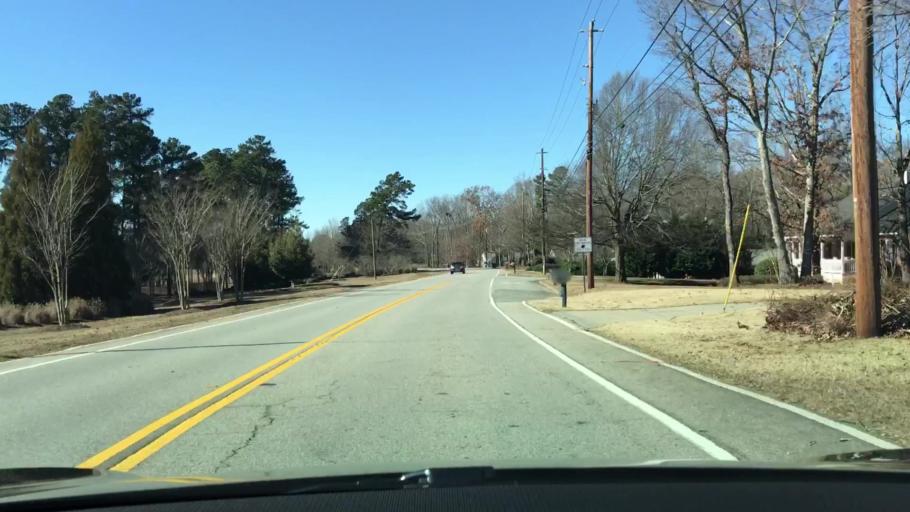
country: US
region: Georgia
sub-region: Gwinnett County
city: Buford
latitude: 34.1434
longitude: -83.9978
